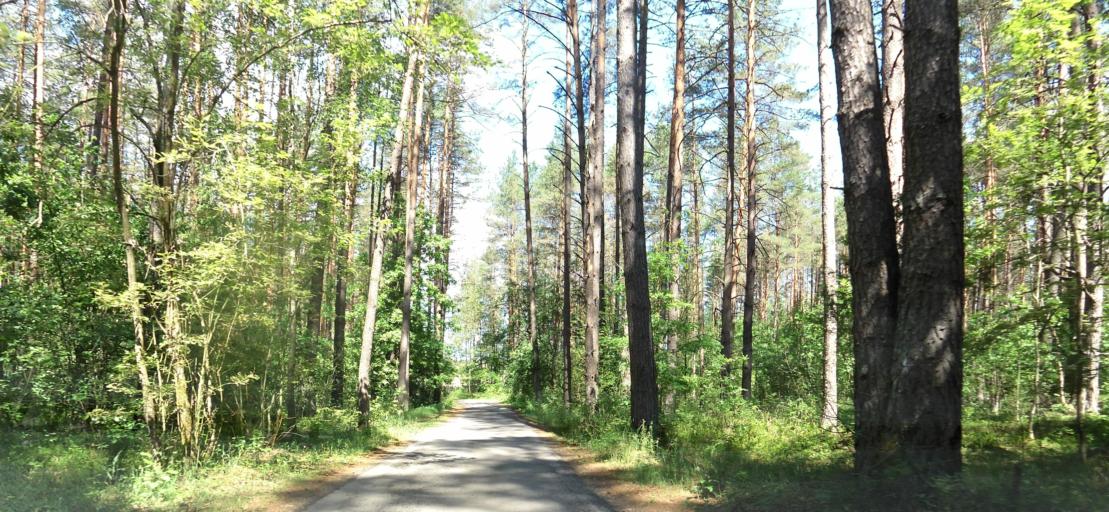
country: LT
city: Nemencine
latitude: 54.8122
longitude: 25.3924
